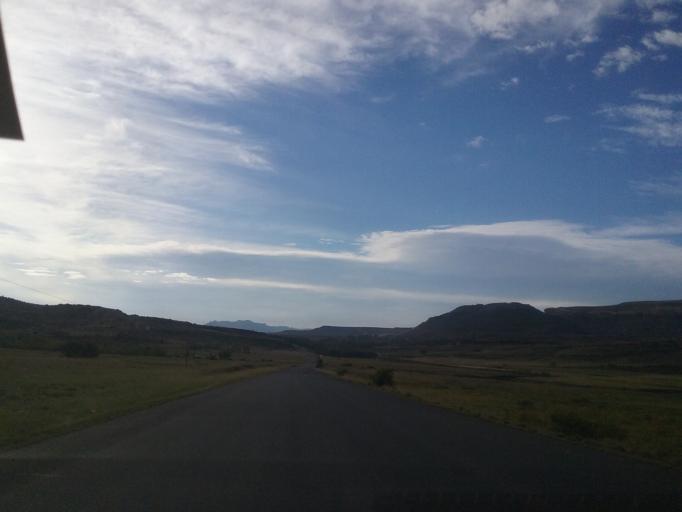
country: LS
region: Quthing
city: Quthing
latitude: -30.3847
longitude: 27.5957
